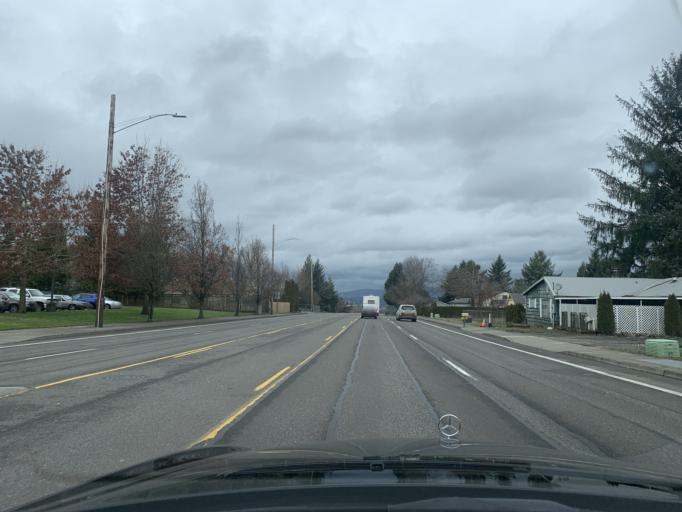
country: US
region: Oregon
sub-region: Multnomah County
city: Troutdale
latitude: 45.5310
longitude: -122.3993
